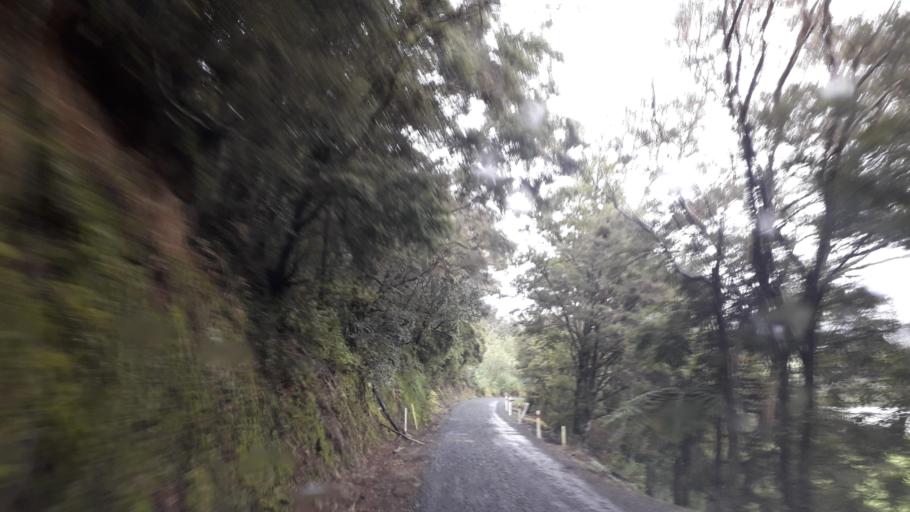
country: NZ
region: Northland
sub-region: Far North District
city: Waimate North
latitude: -35.1482
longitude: 173.7122
